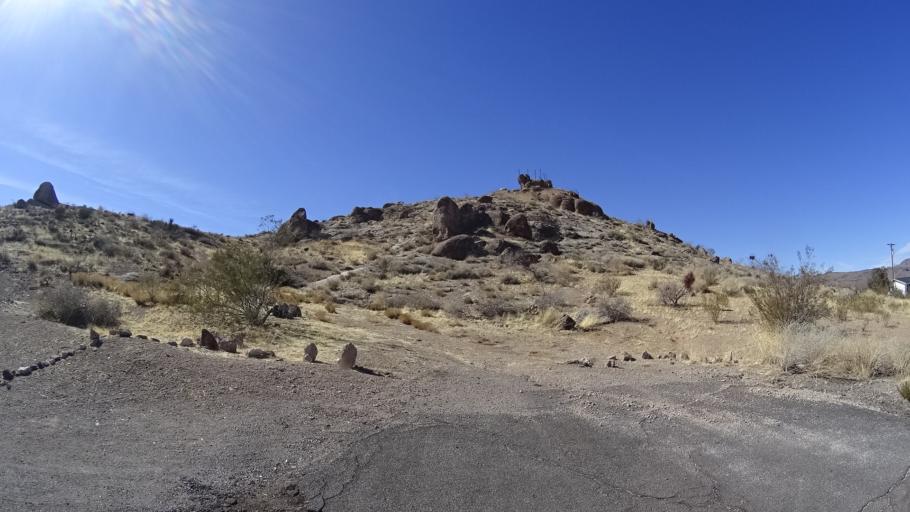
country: US
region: Arizona
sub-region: Mohave County
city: Kingman
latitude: 35.1980
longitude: -114.0359
